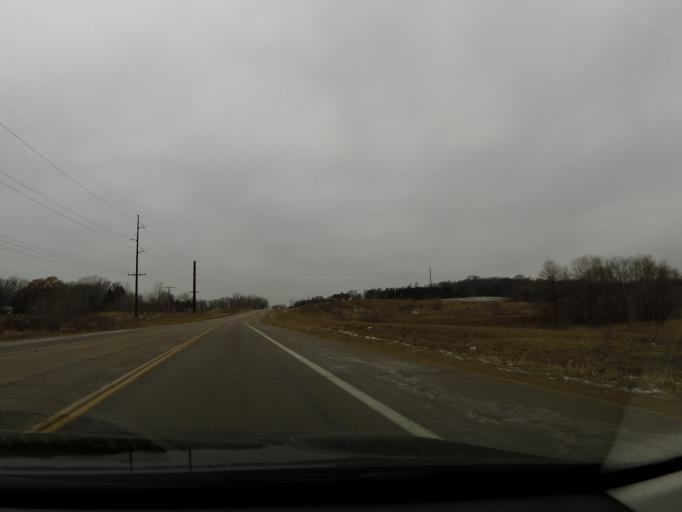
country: US
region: Minnesota
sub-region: Carver County
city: Chaska
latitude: 44.8059
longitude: -93.6385
